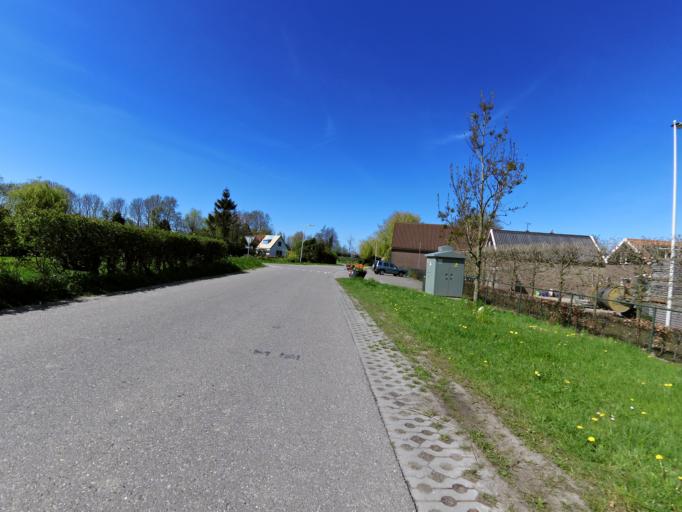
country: NL
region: South Holland
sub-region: Gemeente Brielle
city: Brielle
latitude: 51.8924
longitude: 4.1408
